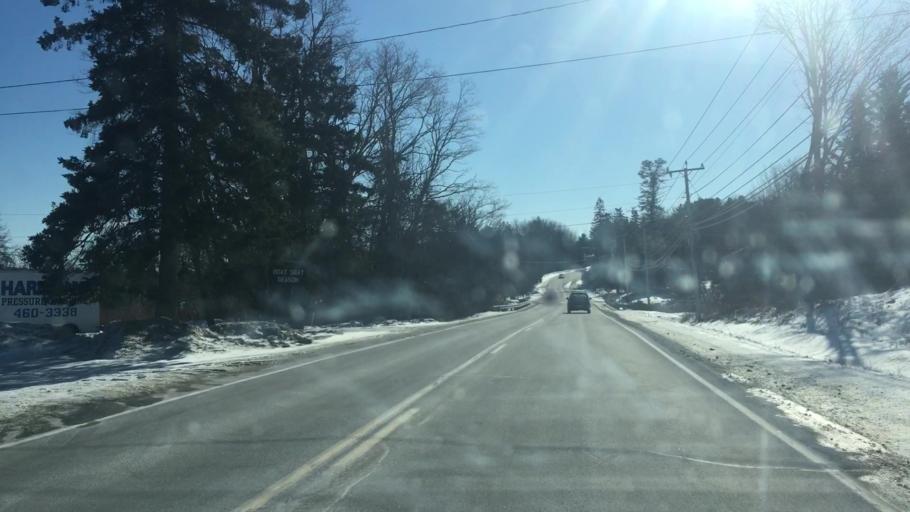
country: US
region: Maine
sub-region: Hancock County
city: Ellsworth
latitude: 44.5232
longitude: -68.4314
